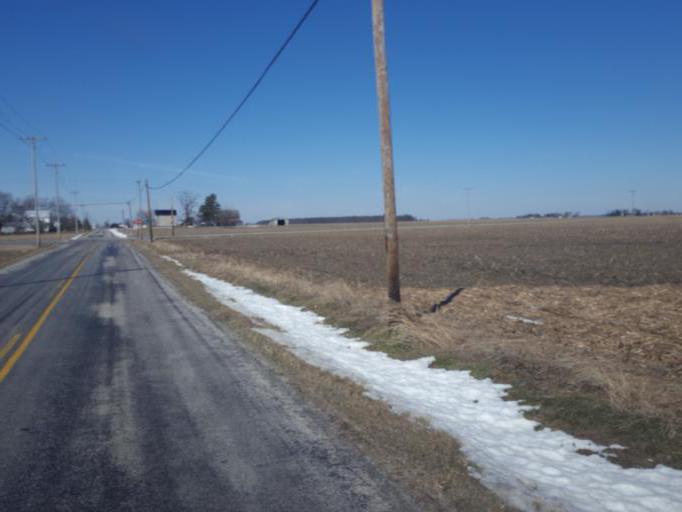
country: US
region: Ohio
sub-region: Marion County
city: Marion
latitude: 40.6588
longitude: -83.2232
